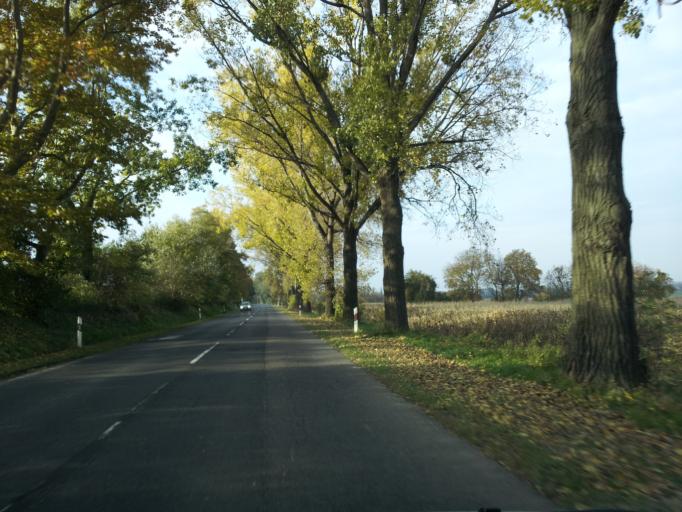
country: HU
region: Gyor-Moson-Sopron
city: Pannonhalma
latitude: 47.5323
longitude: 17.7417
